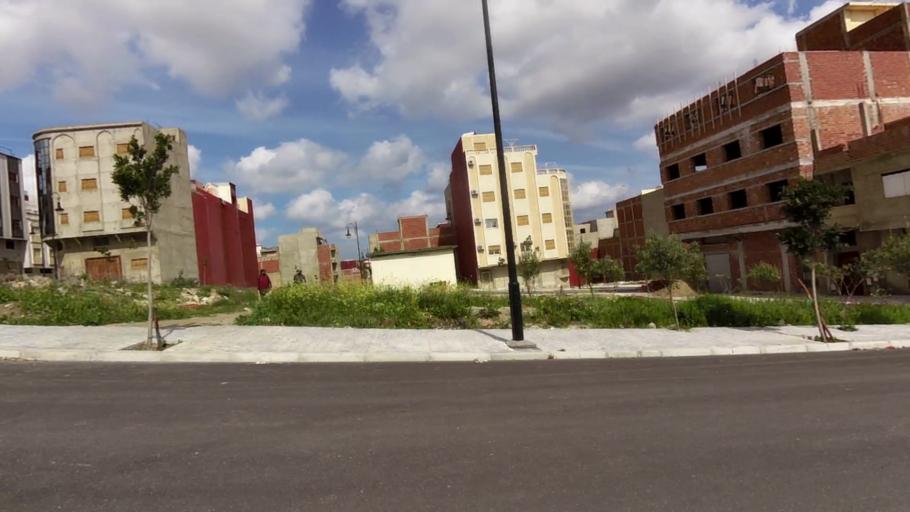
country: MA
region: Tanger-Tetouan
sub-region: Tanger-Assilah
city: Tangier
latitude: 35.7643
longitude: -5.7617
